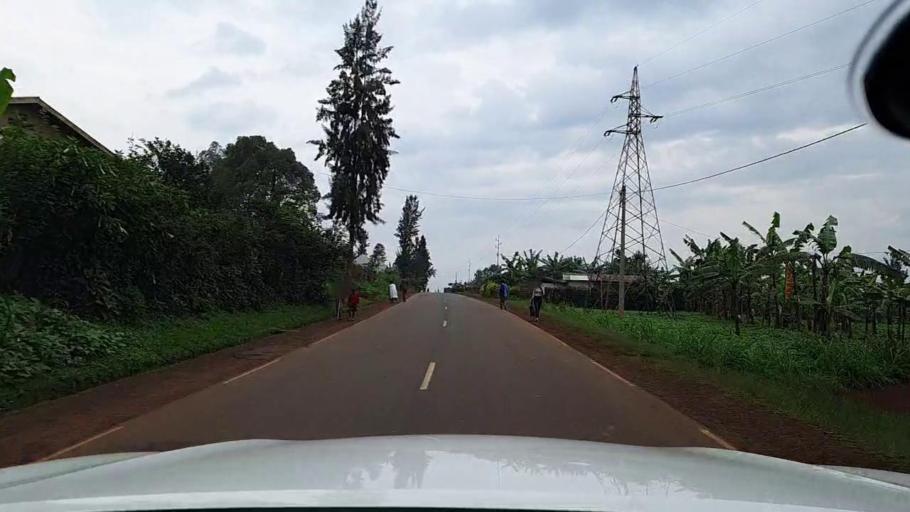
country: RW
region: Western Province
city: Cyangugu
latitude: -2.6184
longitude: 28.9451
